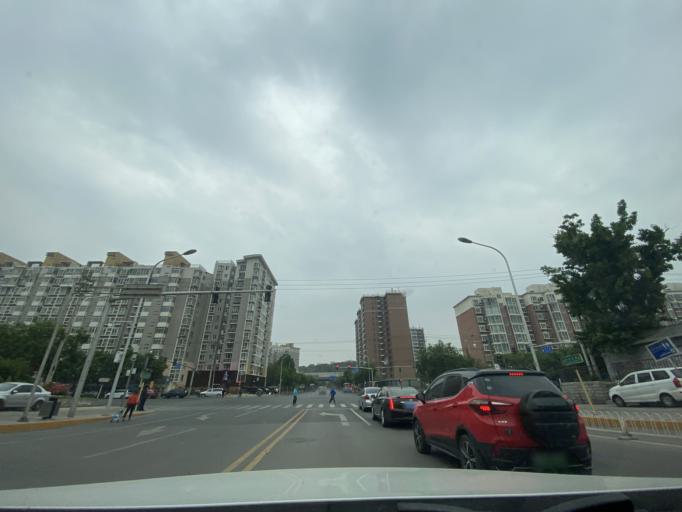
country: CN
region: Beijing
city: Babaoshan
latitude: 39.9287
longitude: 116.2422
